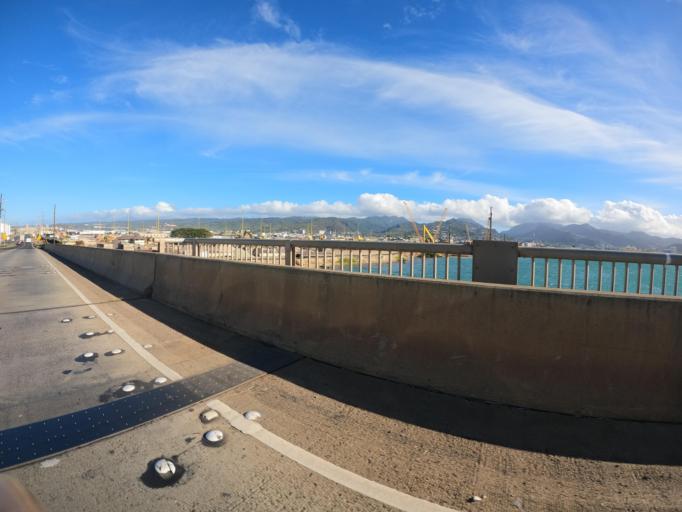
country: US
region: Hawaii
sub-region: Honolulu County
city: Honolulu
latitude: 21.3149
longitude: -157.8881
